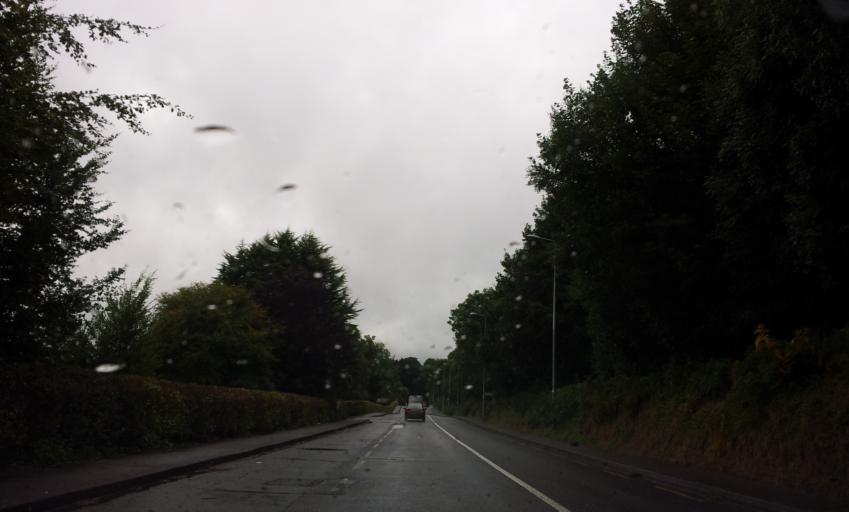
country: IE
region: Munster
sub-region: County Cork
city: Tower
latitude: 51.9271
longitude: -8.6010
